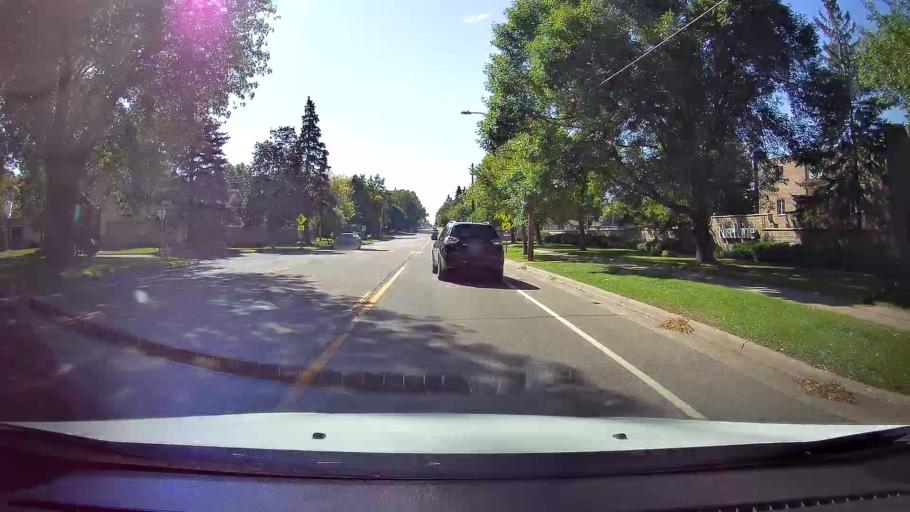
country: US
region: Minnesota
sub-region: Ramsey County
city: Roseville
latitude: 45.0181
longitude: -93.1568
